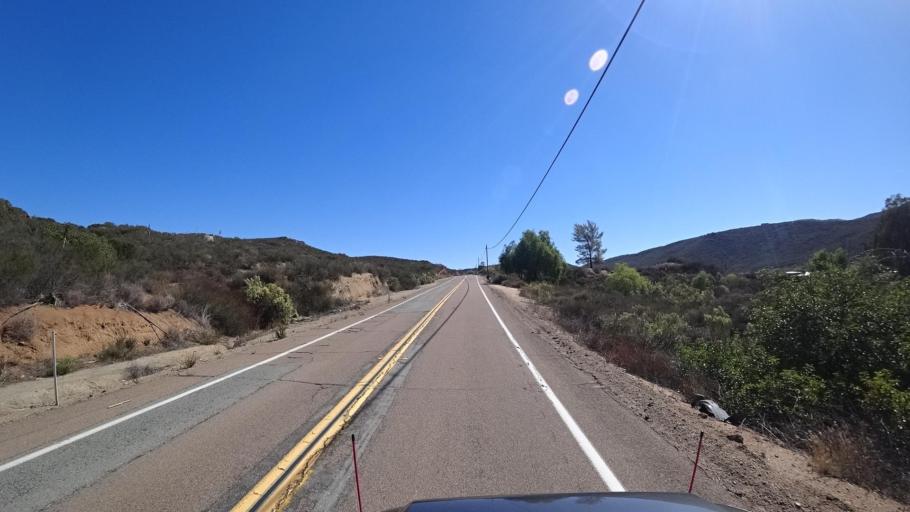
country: US
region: California
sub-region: San Diego County
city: Alpine
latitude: 32.7887
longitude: -116.7297
